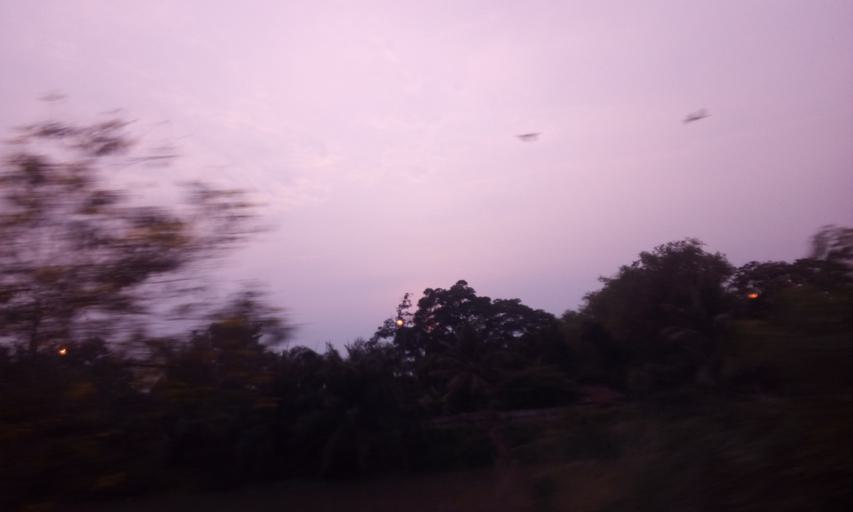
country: TH
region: Pathum Thani
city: Ban Lam Luk Ka
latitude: 14.0269
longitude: 100.8940
